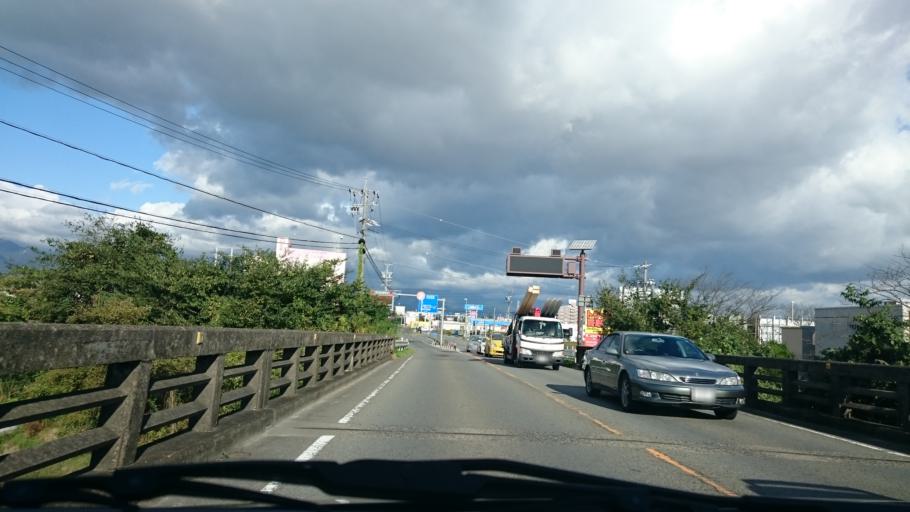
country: JP
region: Mie
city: Komono
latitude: 34.9854
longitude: 136.5544
